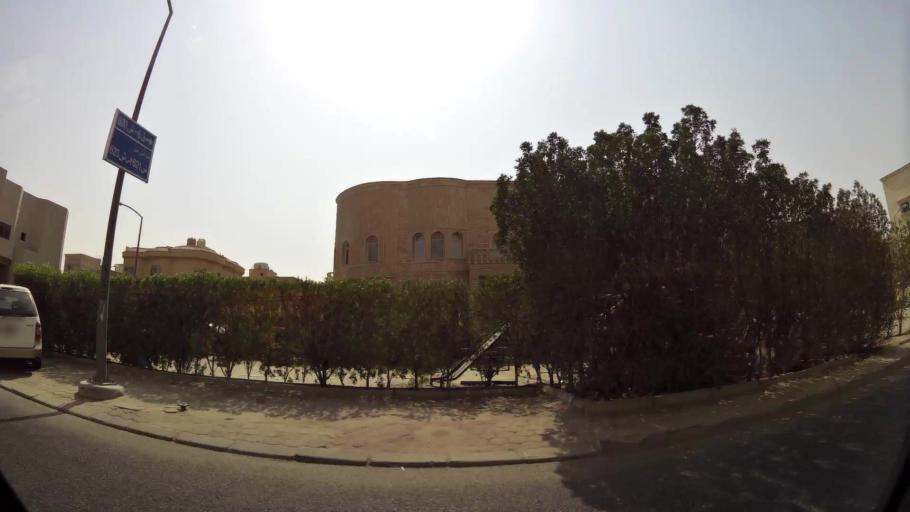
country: KW
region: Muhafazat al Jahra'
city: Al Jahra'
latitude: 29.3049
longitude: 47.6903
